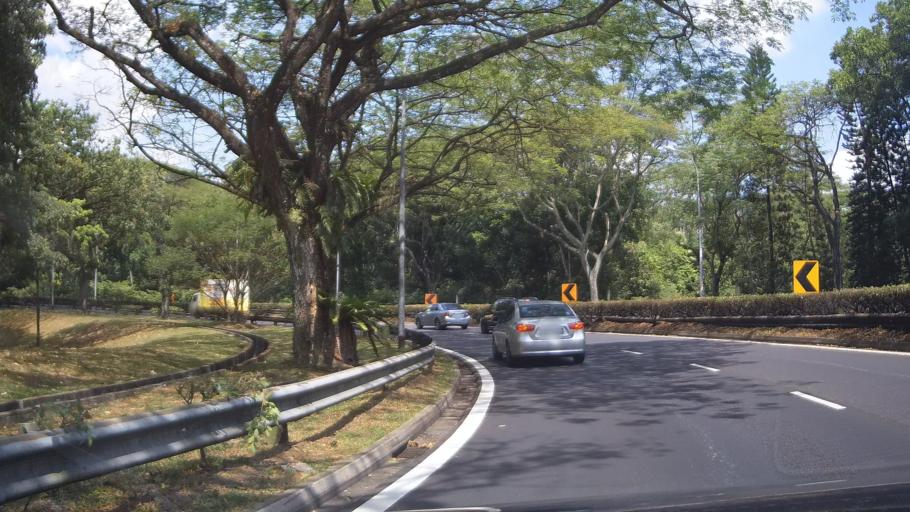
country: SG
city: Singapore
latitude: 1.3338
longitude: 103.7658
